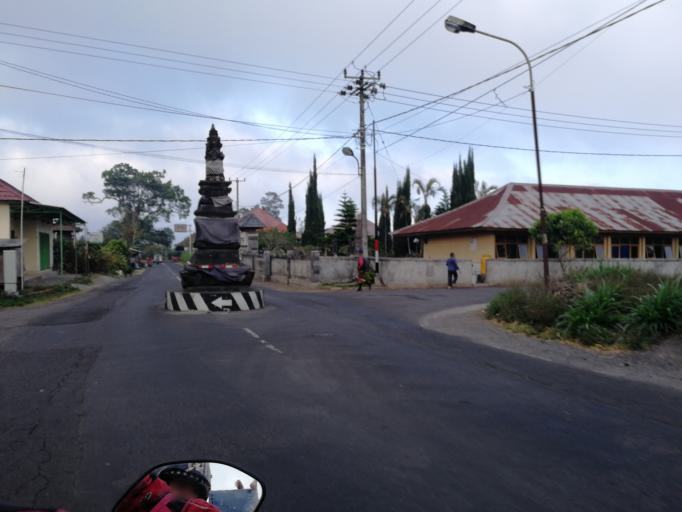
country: ID
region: Bali
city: Banjar Kedisan
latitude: -8.2217
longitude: 115.2684
